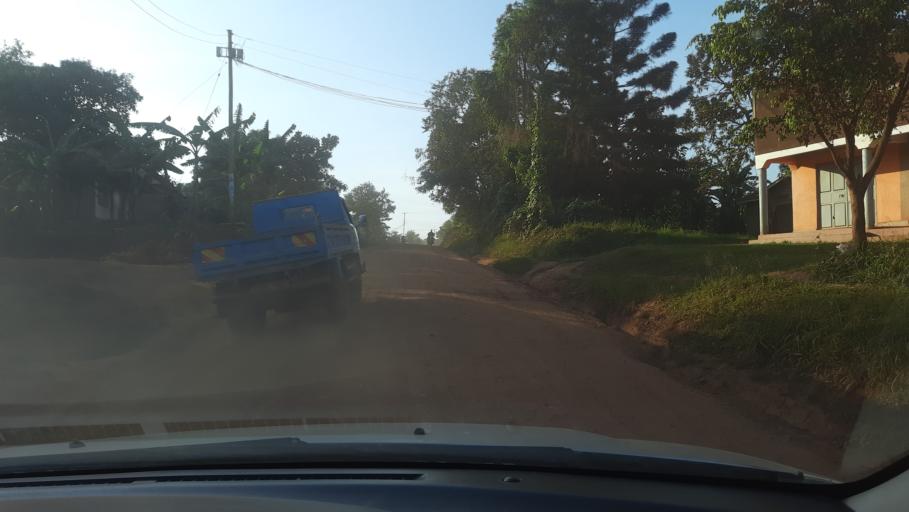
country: UG
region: Central Region
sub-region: Mukono District
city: Mukono
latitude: 0.3715
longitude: 32.7496
